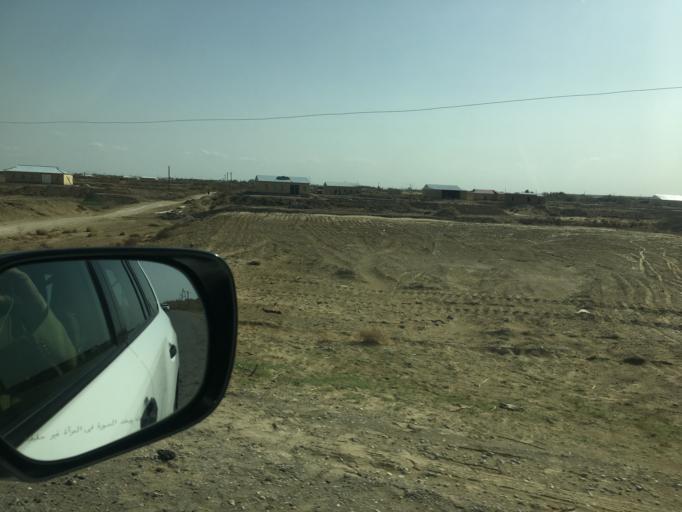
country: TM
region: Lebap
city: Farap
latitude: 39.3091
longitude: 63.3817
